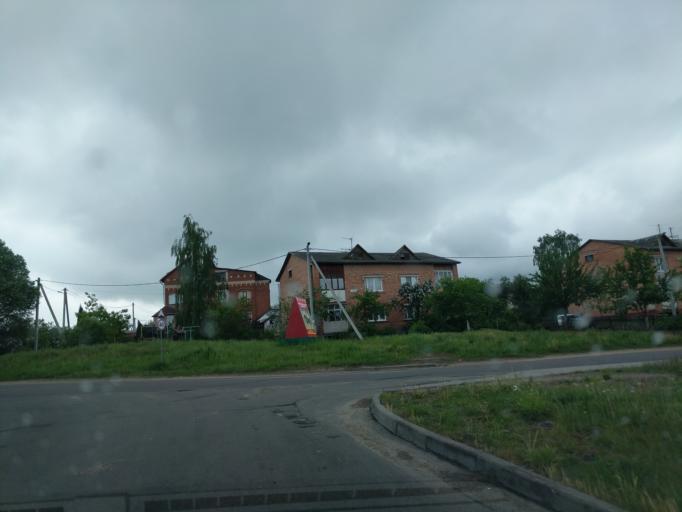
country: BY
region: Minsk
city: Khatsyezhyna
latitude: 53.9360
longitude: 27.3512
